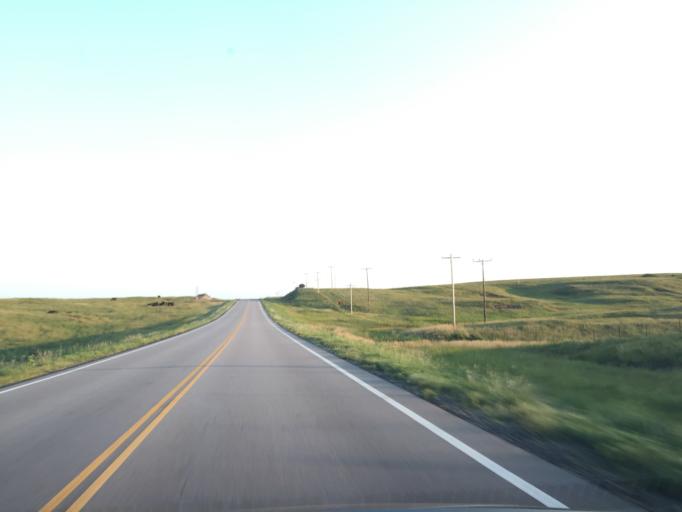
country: US
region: Kansas
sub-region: Ellsworth County
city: Ellsworth
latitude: 38.6411
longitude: -98.2020
